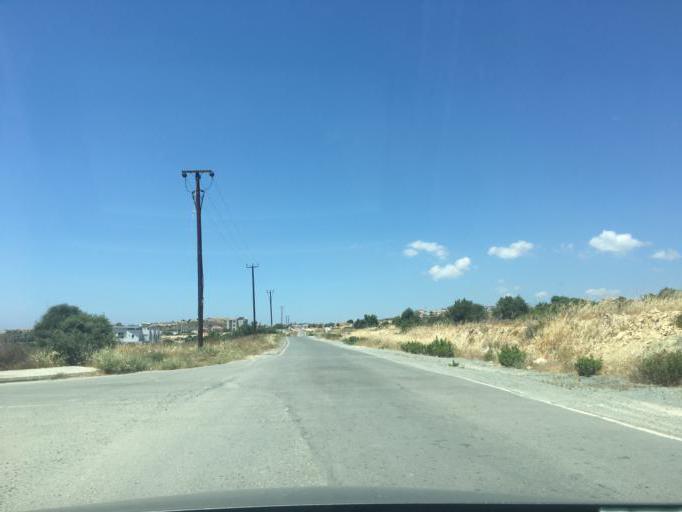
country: CY
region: Limassol
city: Mouttagiaka
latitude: 34.7234
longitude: 33.0725
